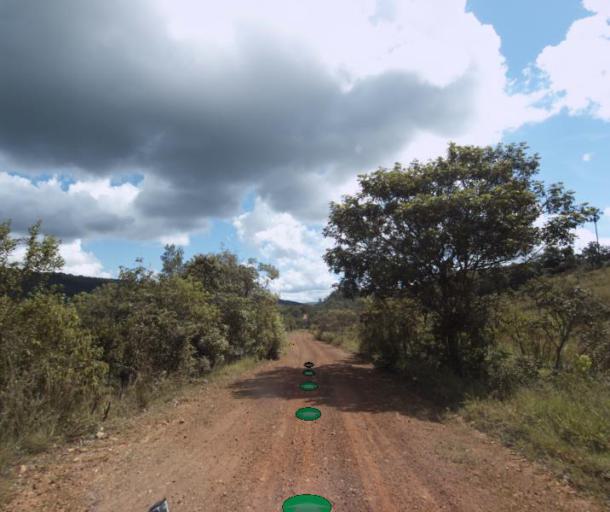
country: BR
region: Goias
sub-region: Pirenopolis
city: Pirenopolis
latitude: -15.7876
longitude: -48.8691
